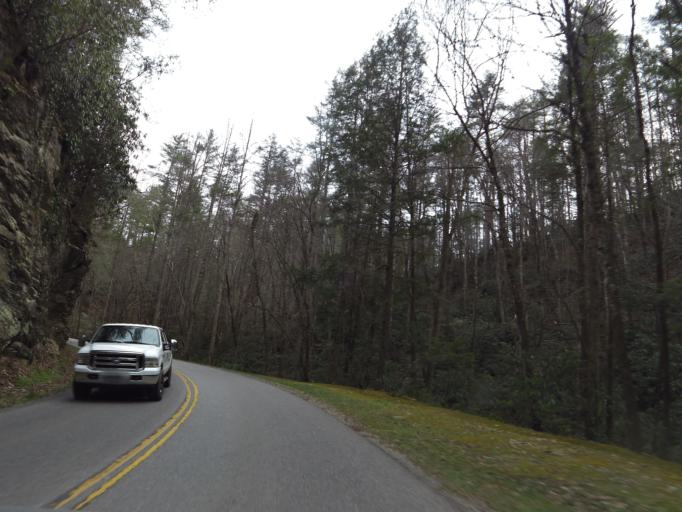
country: US
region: Tennessee
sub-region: Blount County
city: Wildwood
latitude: 35.6327
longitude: -83.7261
